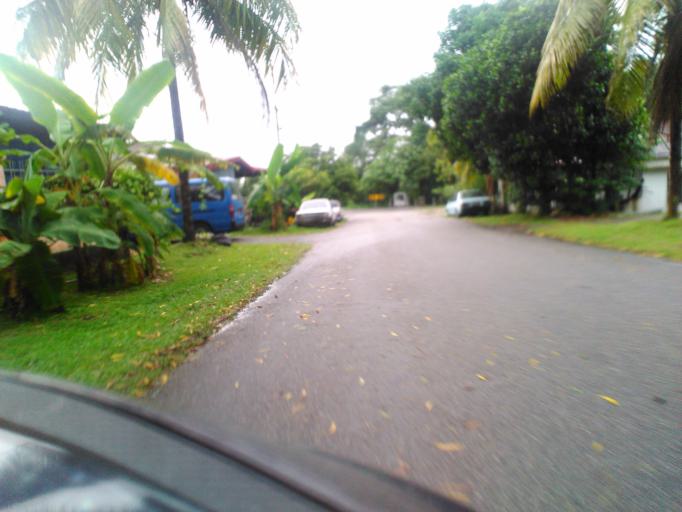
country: MY
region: Kedah
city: Kulim
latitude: 5.3654
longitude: 100.5750
